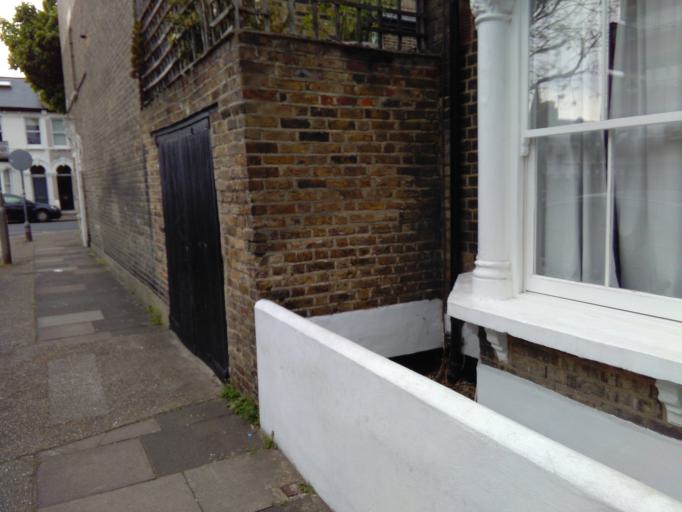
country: GB
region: England
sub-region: Greater London
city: Battersea
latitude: 51.4728
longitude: -0.1697
